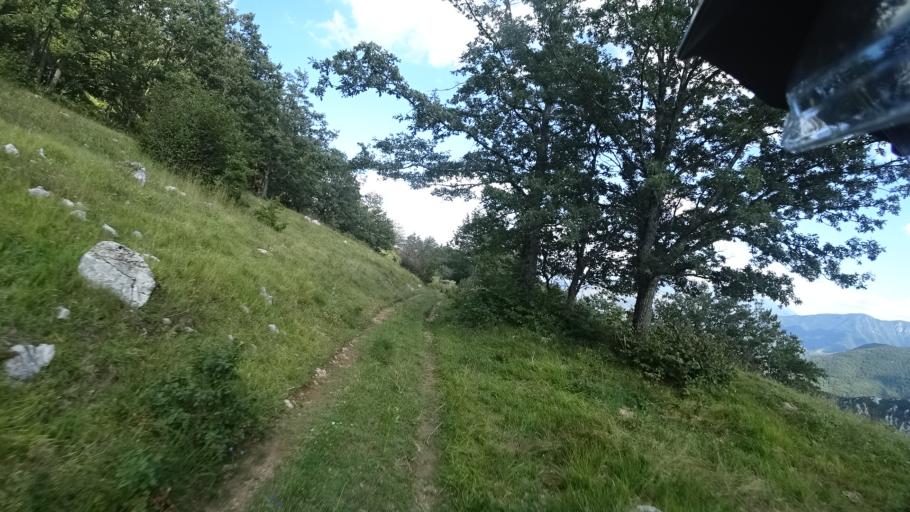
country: HR
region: Zadarska
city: Gracac
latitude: 44.3628
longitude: 16.0800
